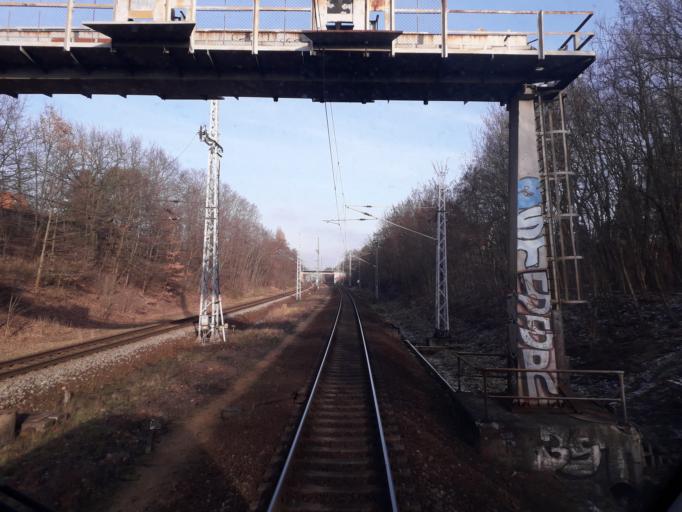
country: DE
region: Berlin
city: Altglienicke
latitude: 52.4112
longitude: 13.5506
